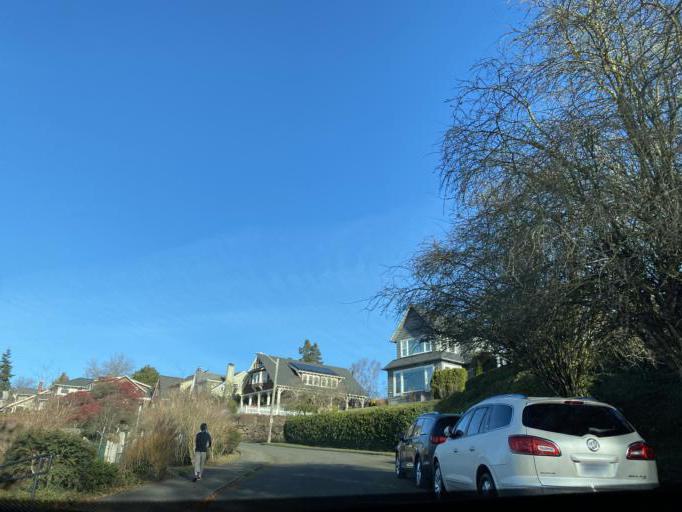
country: US
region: Washington
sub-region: King County
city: Seattle
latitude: 47.6403
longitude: -122.3715
